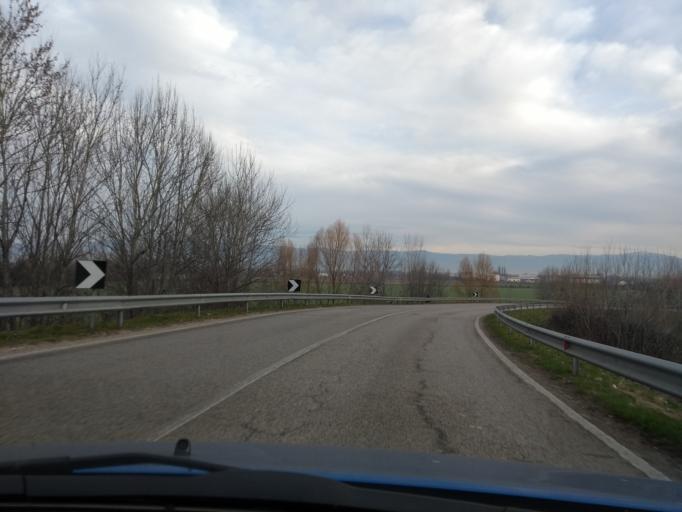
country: IT
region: Veneto
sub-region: Provincia di Vicenza
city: Bolzano Vicentino
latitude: 45.5917
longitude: 11.6335
